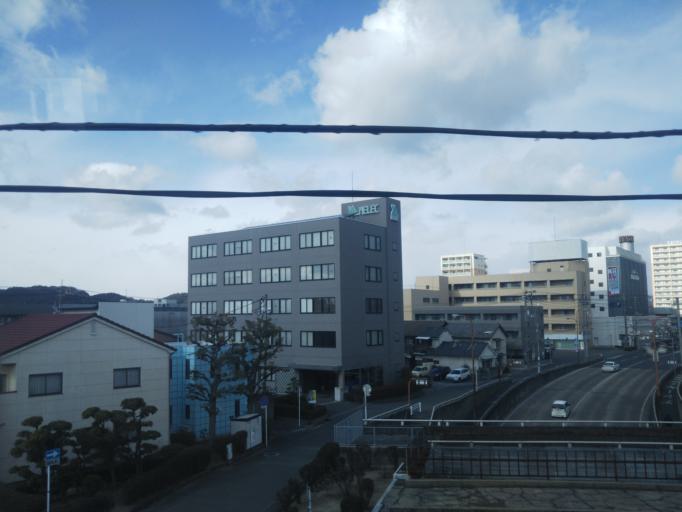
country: JP
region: Okayama
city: Okayama-shi
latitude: 34.6619
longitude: 133.9117
